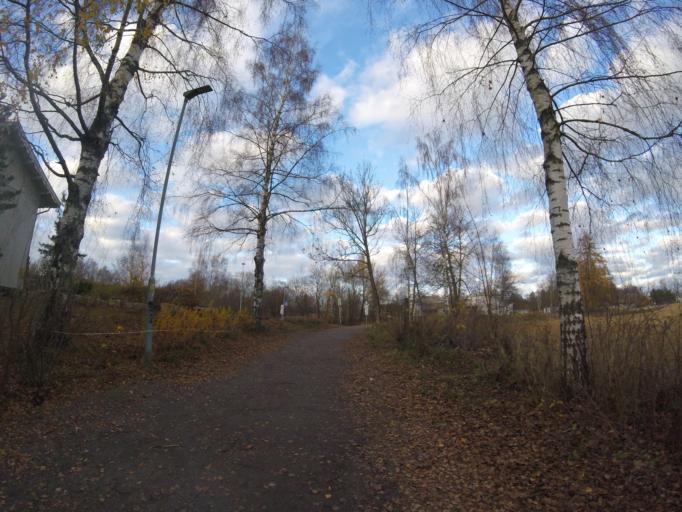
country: NO
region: Akershus
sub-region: Skedsmo
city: Lillestrom
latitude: 59.9930
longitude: 11.0376
